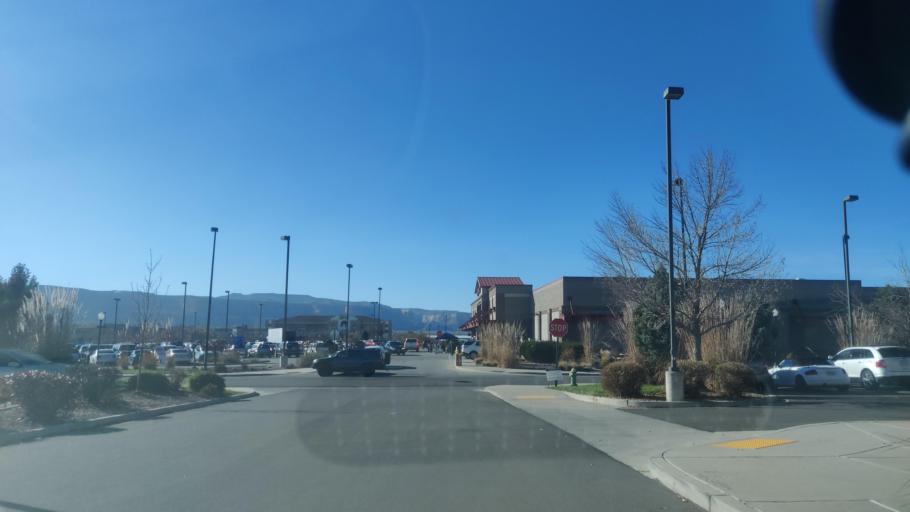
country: US
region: Colorado
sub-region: Mesa County
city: Redlands
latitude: 39.0964
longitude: -108.6058
